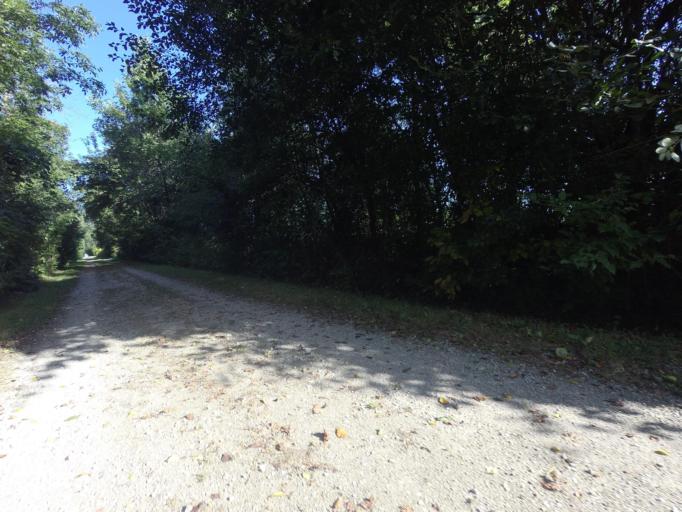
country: CA
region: Ontario
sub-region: Wellington County
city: Guelph
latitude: 43.6622
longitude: -80.4317
